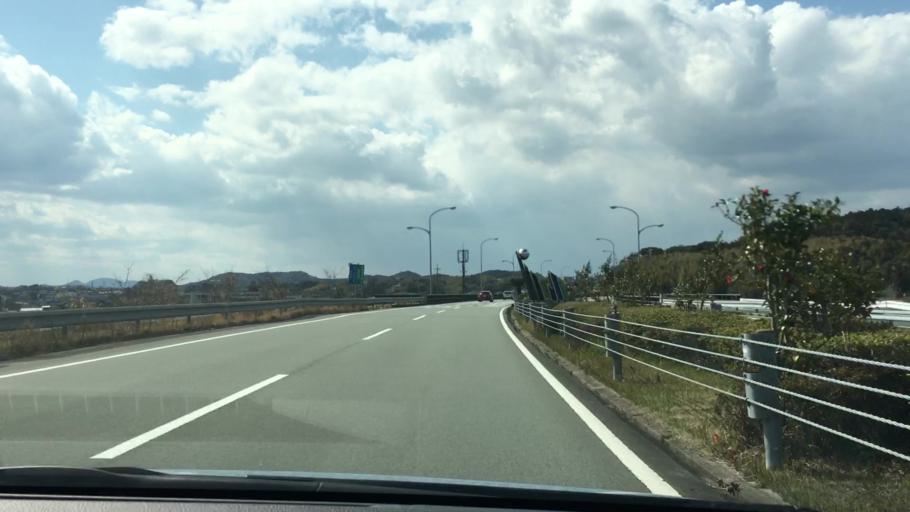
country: JP
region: Mie
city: Ise
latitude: 34.4790
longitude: 136.7416
